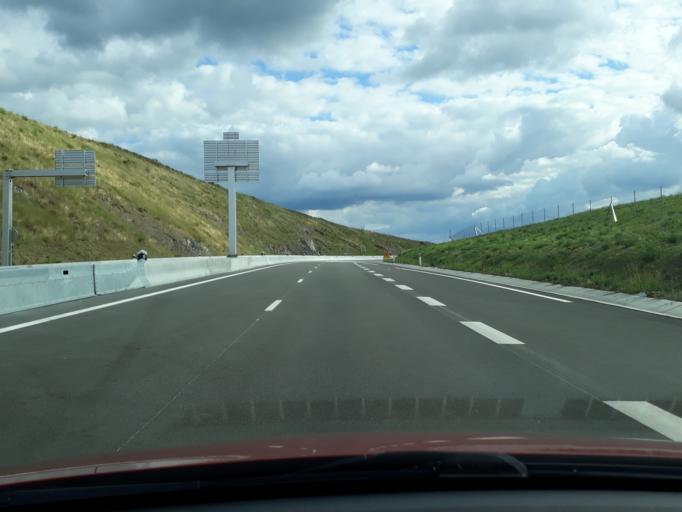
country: FR
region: Auvergne
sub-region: Departement de la Haute-Loire
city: Vals-pres-le-Puy
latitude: 45.0226
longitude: 3.9010
